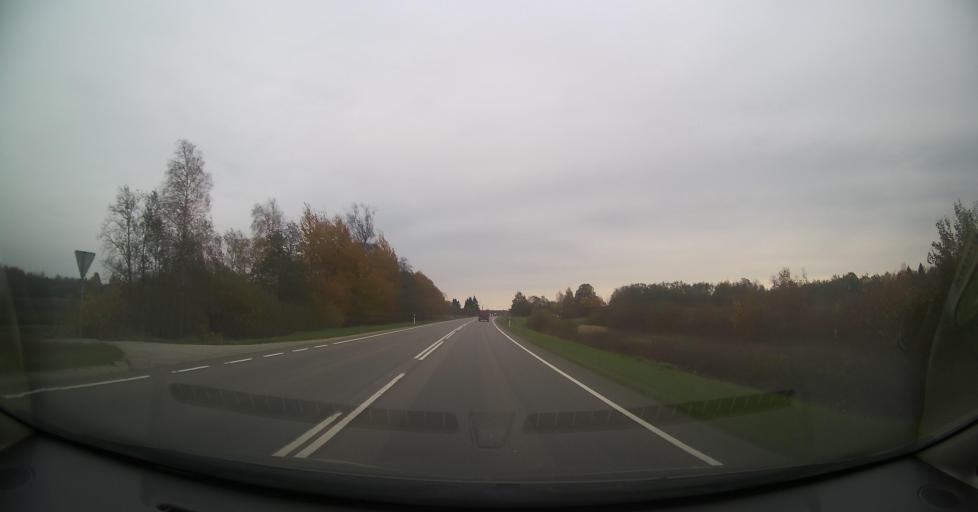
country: EE
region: Laeaene
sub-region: Ridala Parish
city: Uuemoisa
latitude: 58.9735
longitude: 23.8540
